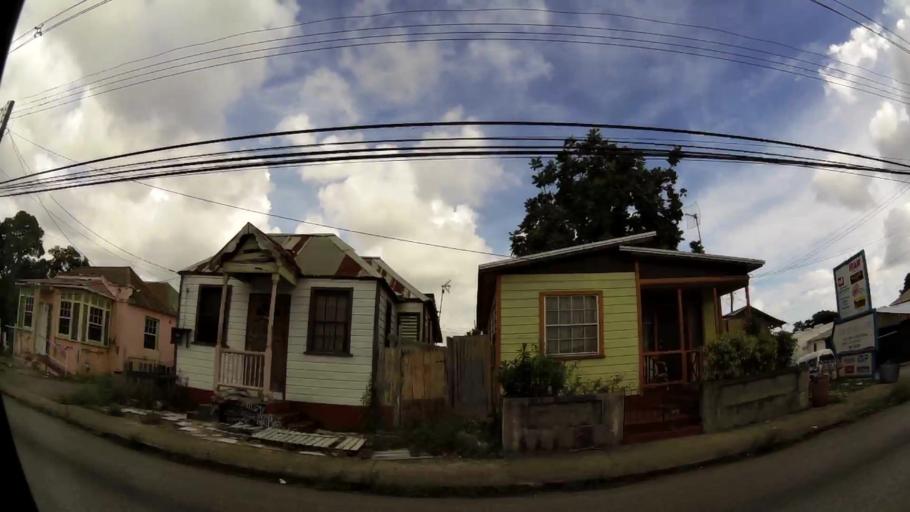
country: BB
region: Saint Michael
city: Bridgetown
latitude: 13.1060
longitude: -59.6056
